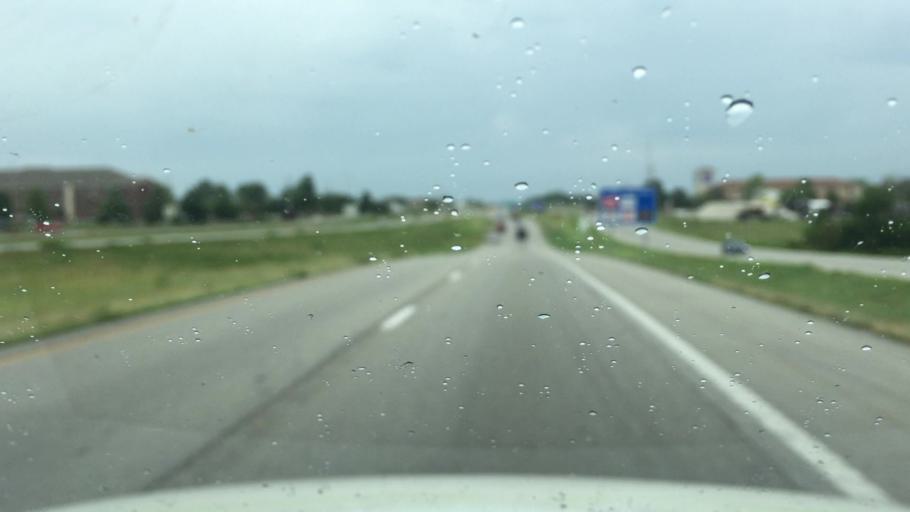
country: US
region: Missouri
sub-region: Jackson County
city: Lees Summit
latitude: 38.9027
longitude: -94.3504
